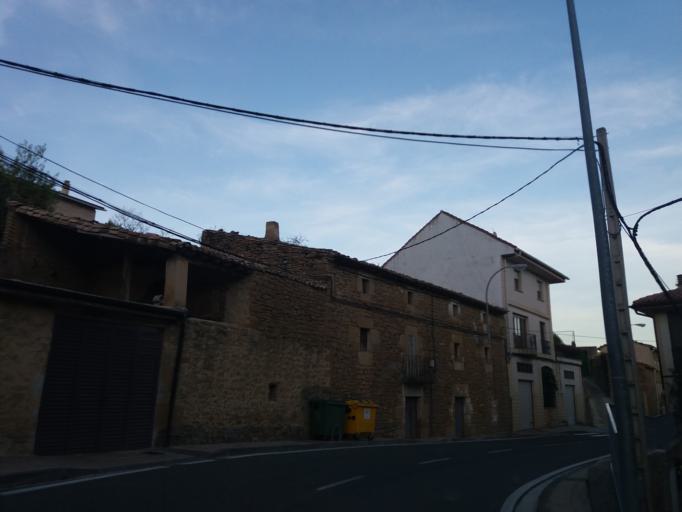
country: ES
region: Navarre
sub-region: Provincia de Navarra
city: San Martin de Unx
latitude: 42.5256
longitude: -1.5587
